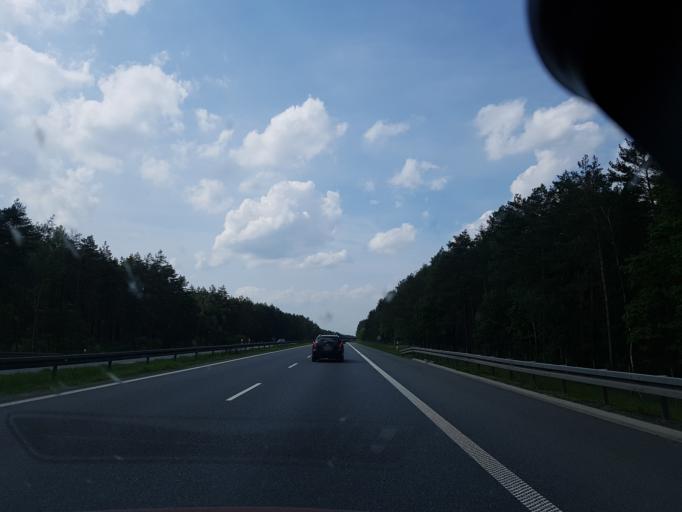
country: PL
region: Opole Voivodeship
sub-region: Powiat opolski
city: Dabrowa
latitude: 50.6250
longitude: 17.7551
